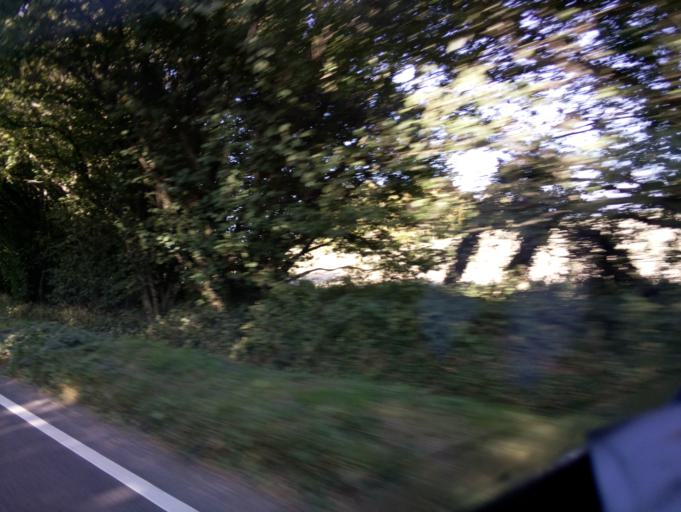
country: GB
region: England
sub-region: Hampshire
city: Alton
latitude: 51.1156
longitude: -0.9956
